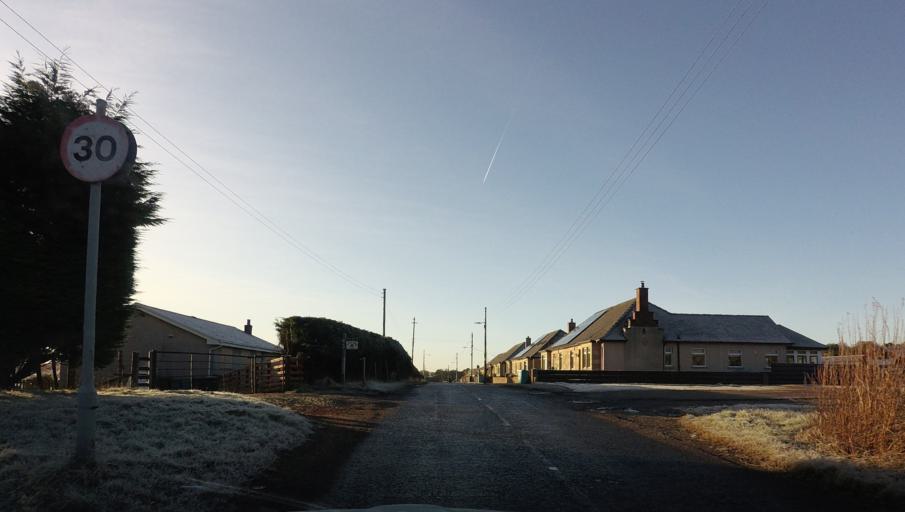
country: GB
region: Scotland
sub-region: North Lanarkshire
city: Shotts
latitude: 55.8139
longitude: -3.8351
